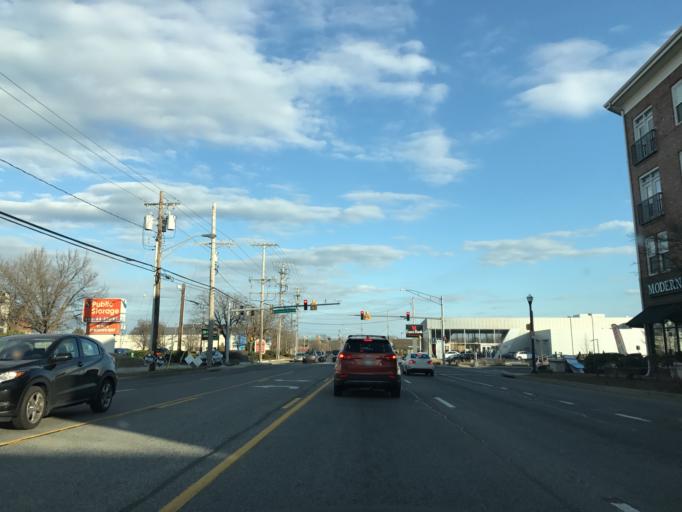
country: US
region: Maryland
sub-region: Anne Arundel County
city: Parole
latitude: 38.9800
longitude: -76.5241
